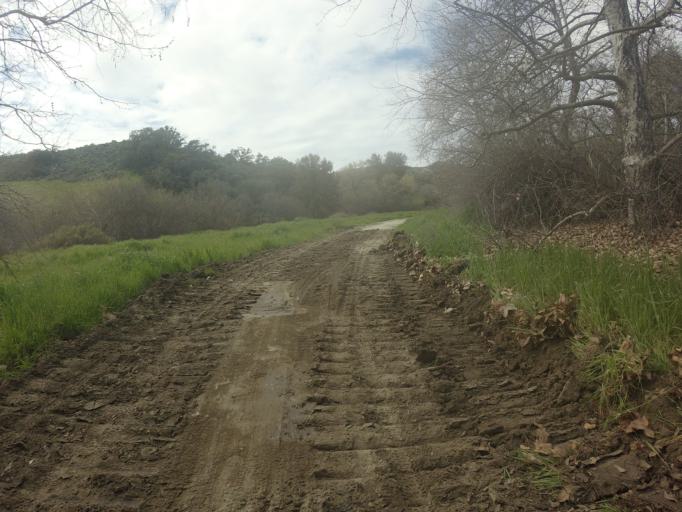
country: US
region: California
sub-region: Orange County
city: Aliso Viejo
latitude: 33.5596
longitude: -117.7423
